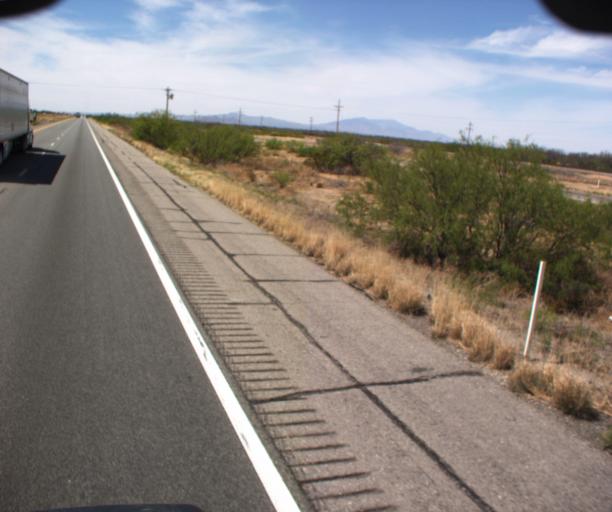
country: US
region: Arizona
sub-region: Cochise County
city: Willcox
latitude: 32.3015
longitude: -109.3717
